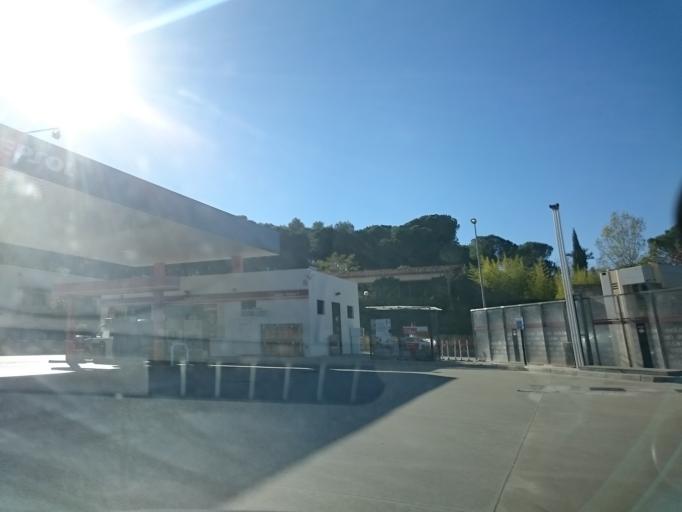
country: ES
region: Catalonia
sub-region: Provincia de Barcelona
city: Capellades
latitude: 41.5369
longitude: 1.6799
